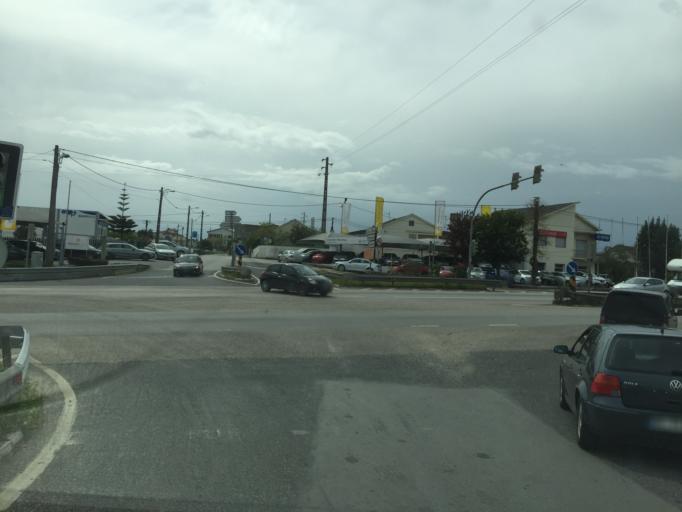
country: PT
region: Leiria
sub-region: Leiria
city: Caranguejeira
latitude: 39.8267
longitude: -8.7238
